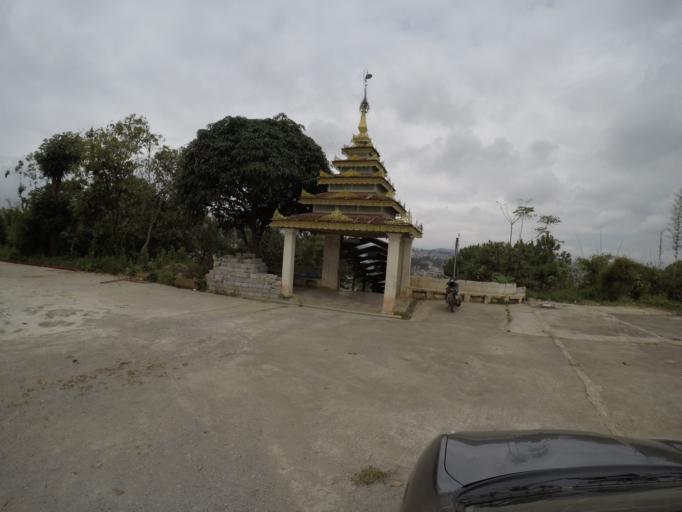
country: MM
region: Shan
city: Taunggyi
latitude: 20.6503
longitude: 96.6418
